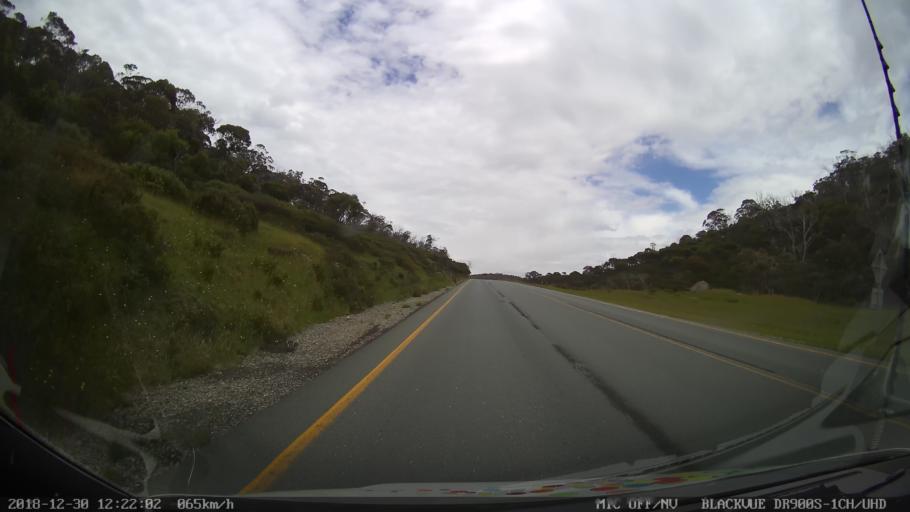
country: AU
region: New South Wales
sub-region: Snowy River
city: Jindabyne
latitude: -36.3563
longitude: 148.5136
